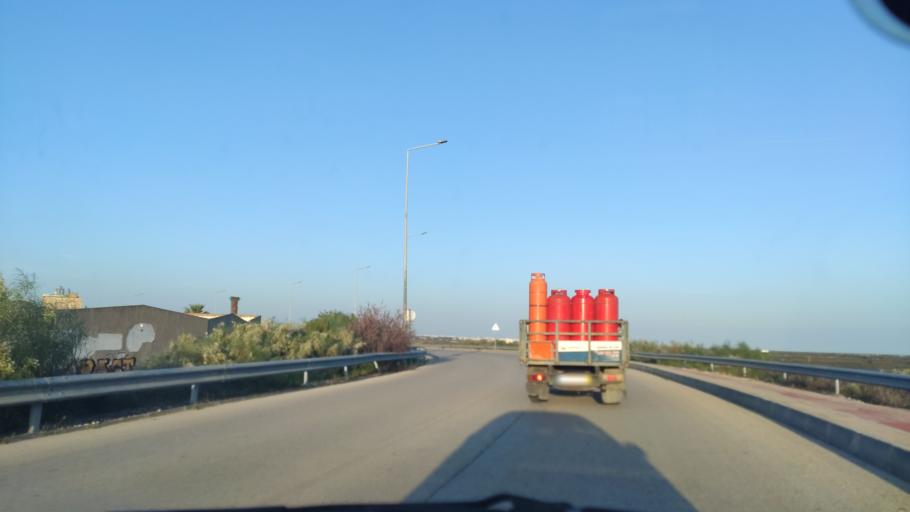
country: PT
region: Faro
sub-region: Faro
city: Faro
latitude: 37.0110
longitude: -7.9189
